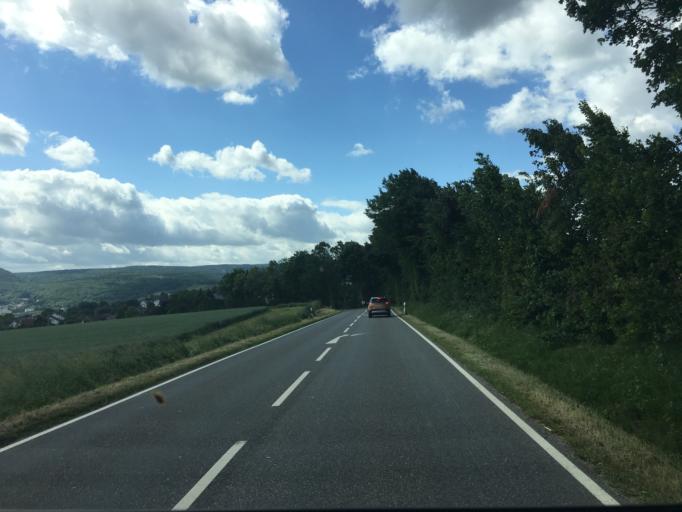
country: DE
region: Rheinland-Pfalz
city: Bad Neuenahr-Ahrweiler
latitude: 50.5620
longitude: 7.1064
